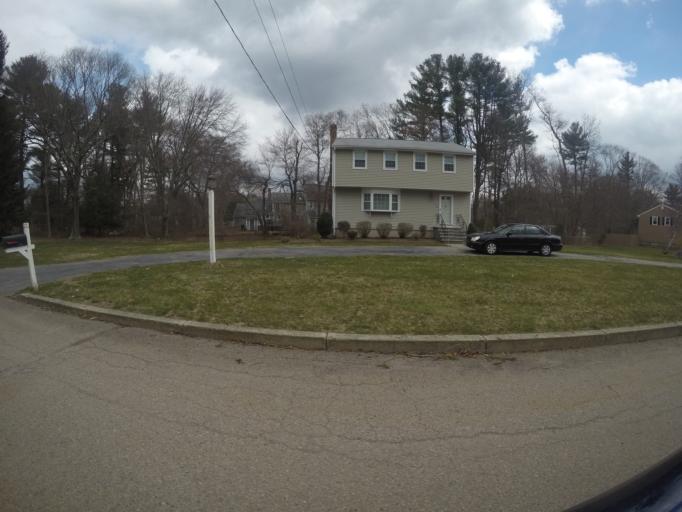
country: US
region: Massachusetts
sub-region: Bristol County
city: Easton
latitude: 42.0490
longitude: -71.1321
